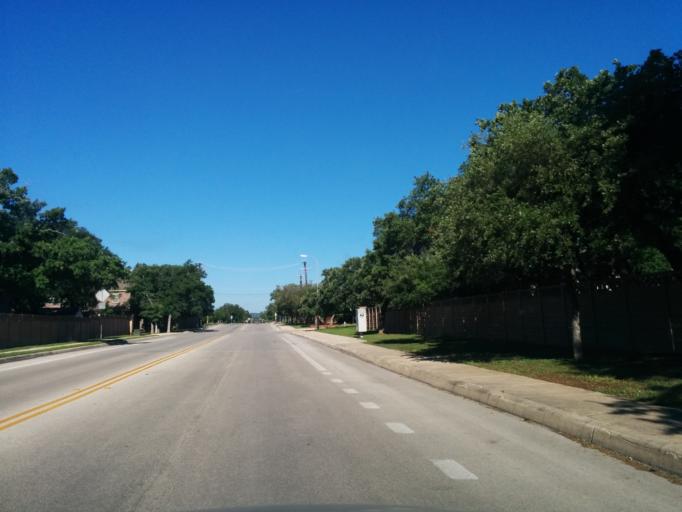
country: US
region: Texas
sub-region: Bexar County
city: Cross Mountain
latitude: 29.6720
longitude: -98.6431
